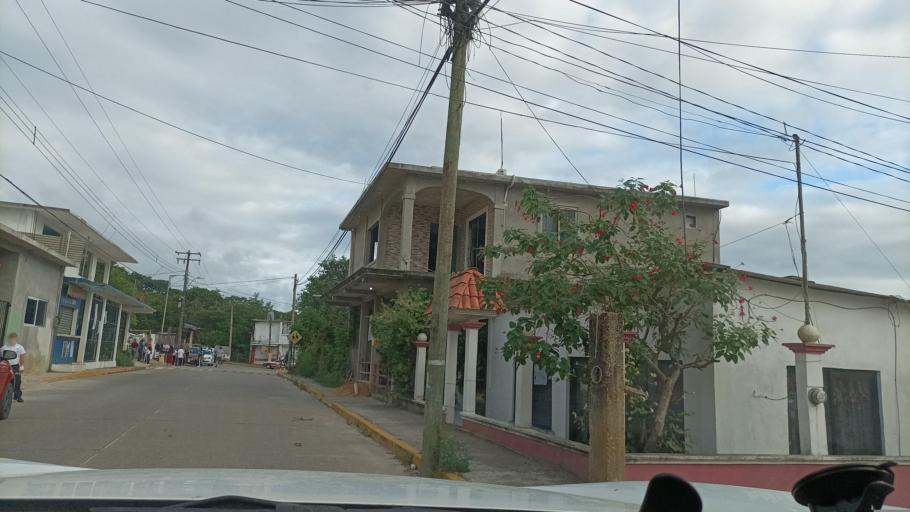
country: MX
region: Veracruz
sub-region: Cosoleacaque
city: Hermenegildo J. Aldana
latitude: 17.9966
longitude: -94.6113
